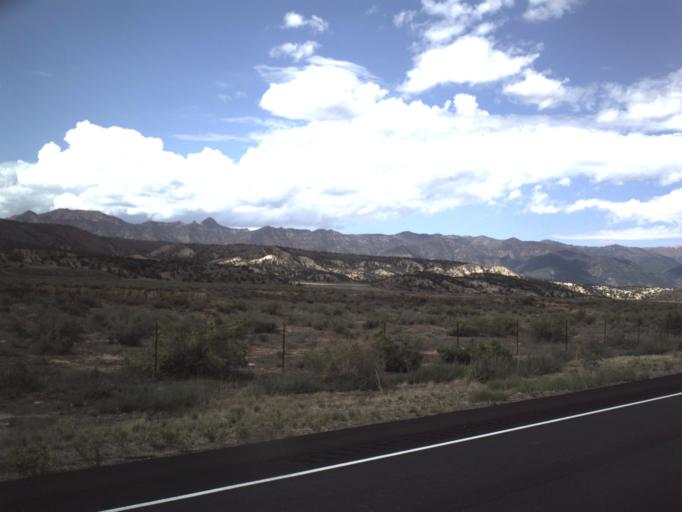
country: US
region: Utah
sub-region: Sevier County
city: Aurora
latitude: 38.9701
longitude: -111.9527
